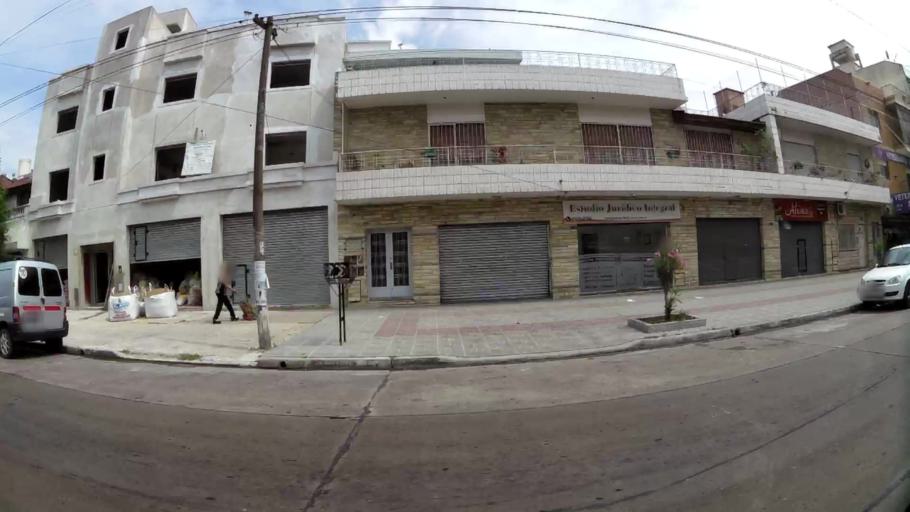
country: AR
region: Buenos Aires F.D.
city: Villa Lugano
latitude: -34.6942
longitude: -58.5025
